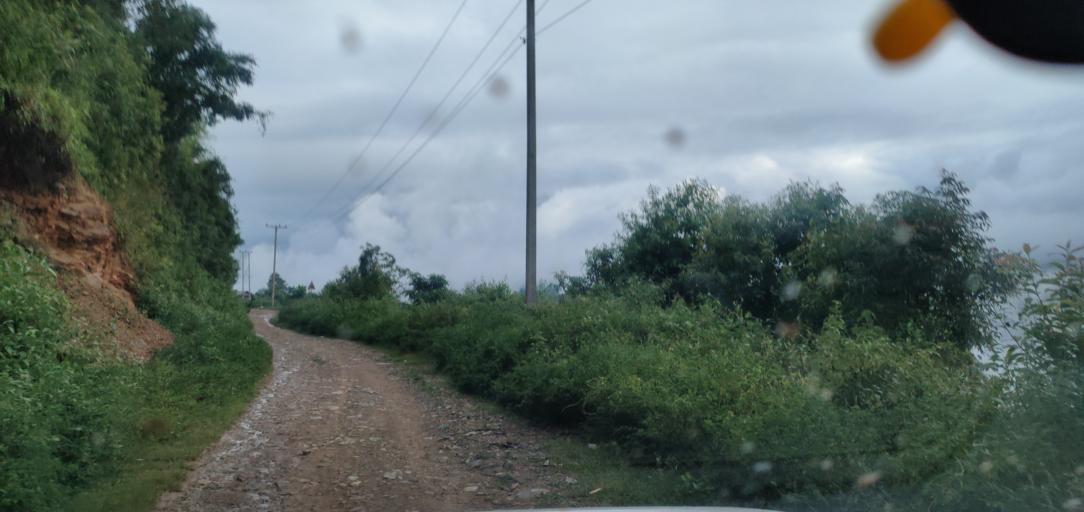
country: LA
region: Phongsali
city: Phongsali
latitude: 21.4429
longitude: 102.2939
